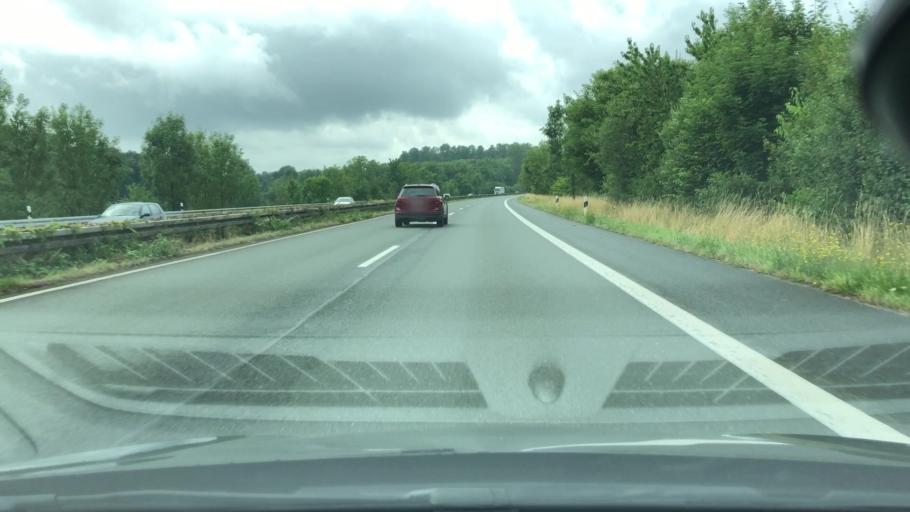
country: DE
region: Lower Saxony
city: Buckeburg
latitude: 52.2616
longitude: 8.9878
